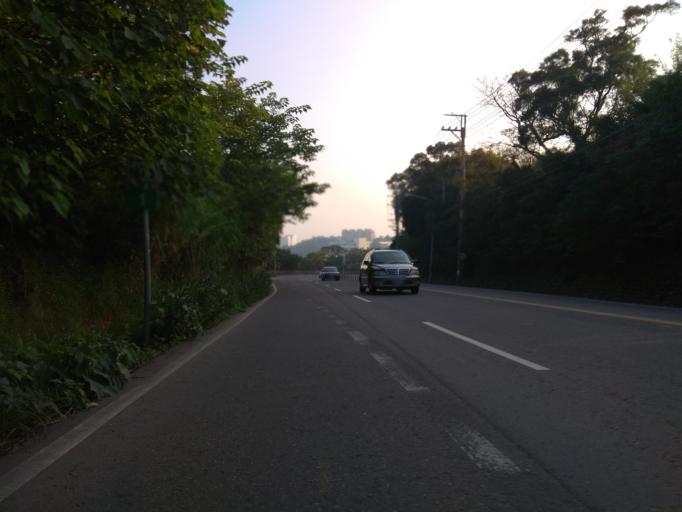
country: TW
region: Taiwan
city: Daxi
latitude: 24.9110
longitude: 121.1884
